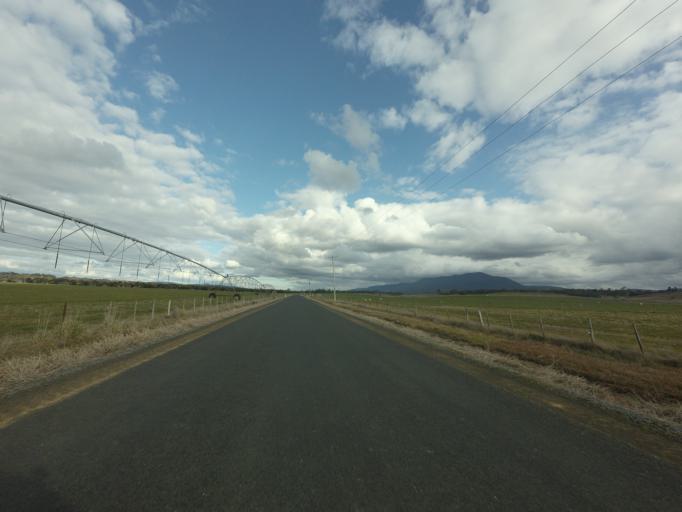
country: AU
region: Tasmania
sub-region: Northern Midlands
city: Longford
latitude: -41.8231
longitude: 147.2033
